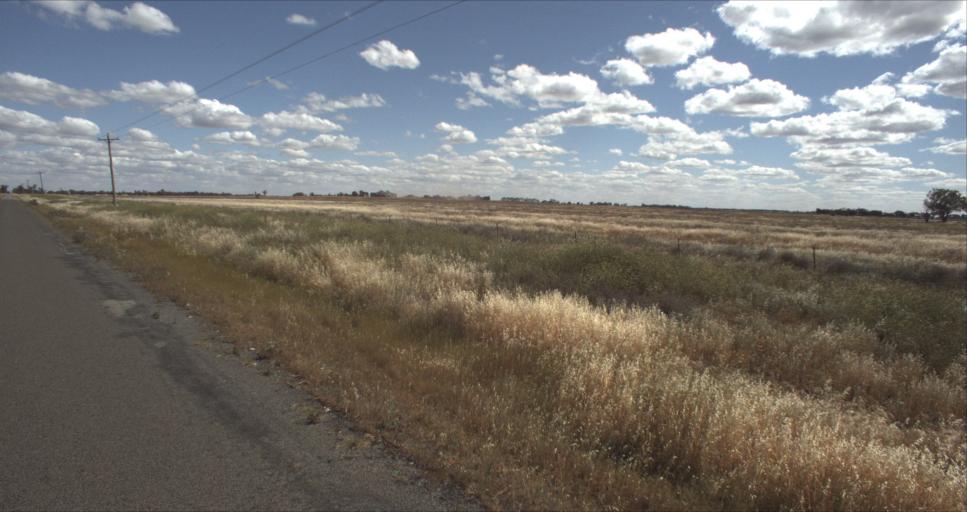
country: AU
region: New South Wales
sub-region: Leeton
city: Leeton
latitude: -34.4718
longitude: 146.2508
